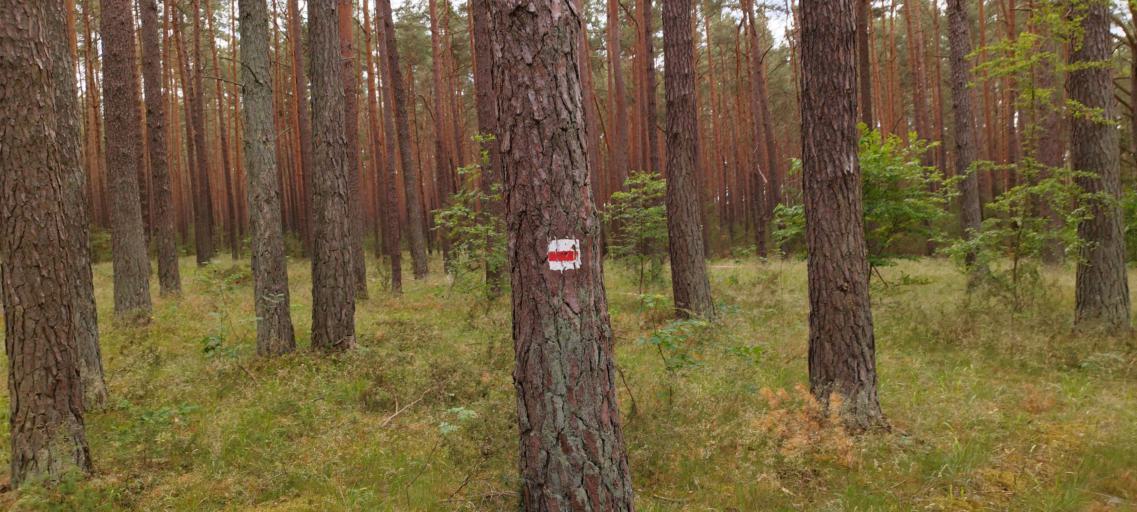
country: DE
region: Brandenburg
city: Grunheide
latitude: 52.4418
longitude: 13.8811
